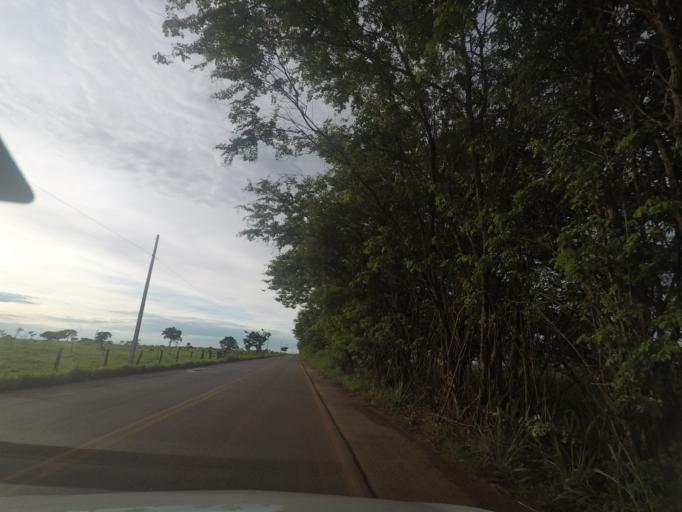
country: BR
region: Goias
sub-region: Trindade
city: Trindade
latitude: -16.7239
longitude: -49.4275
